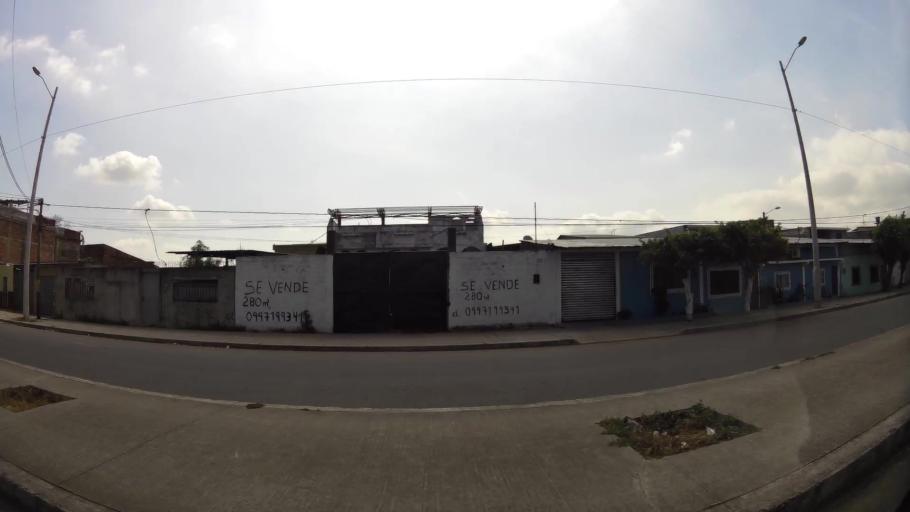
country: EC
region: Guayas
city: Eloy Alfaro
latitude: -2.1652
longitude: -79.8376
